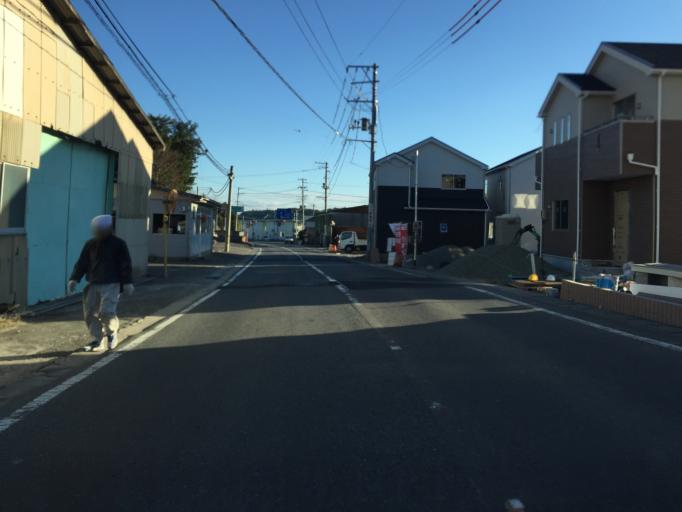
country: JP
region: Fukushima
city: Iwaki
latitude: 37.0881
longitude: 140.8617
